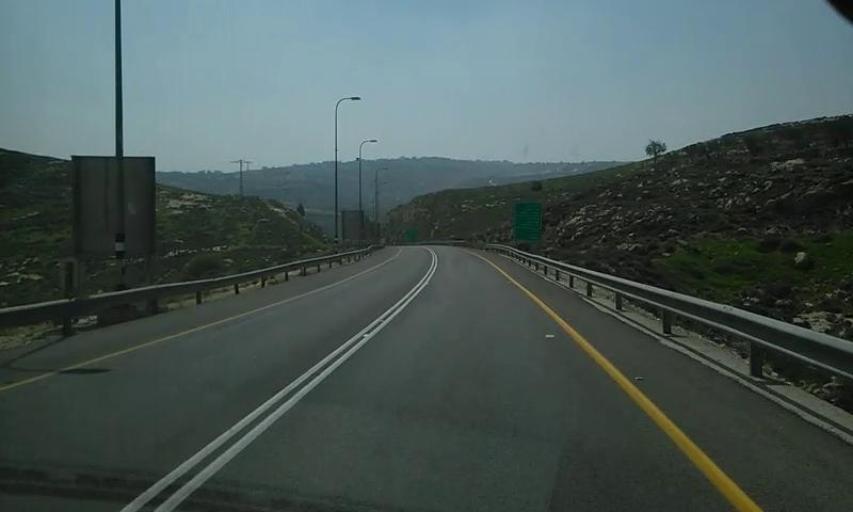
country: PS
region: West Bank
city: Mikhmas
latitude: 31.8772
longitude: 35.2662
